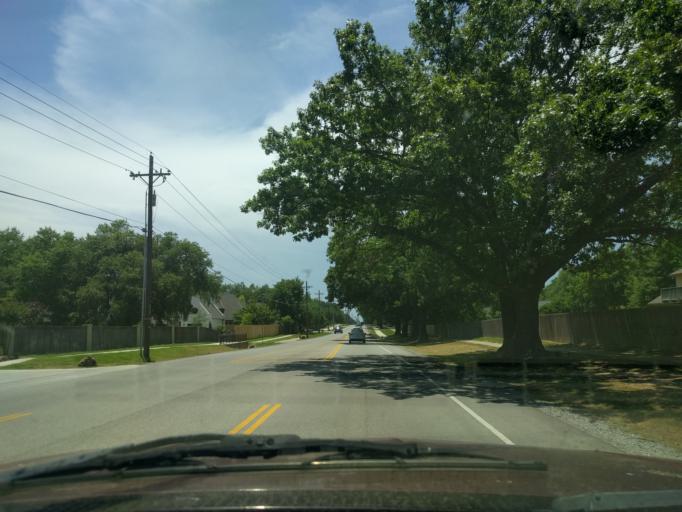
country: US
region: Oklahoma
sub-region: Tulsa County
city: Jenks
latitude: 36.0134
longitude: -95.9222
